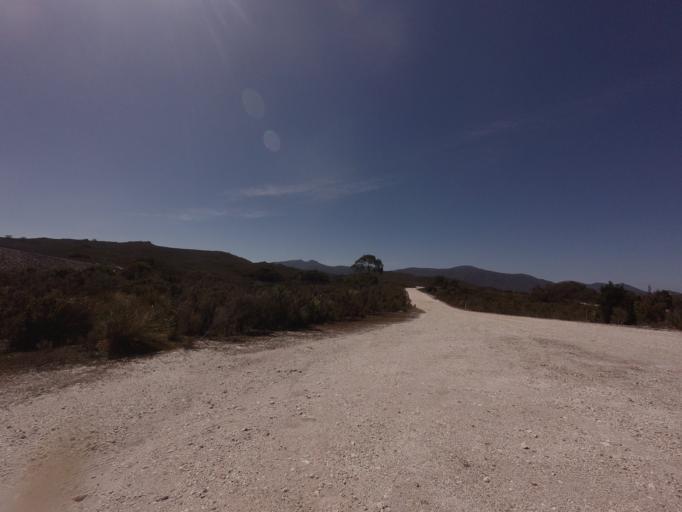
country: AU
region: Tasmania
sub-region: Huon Valley
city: Geeveston
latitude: -43.0308
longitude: 146.3019
